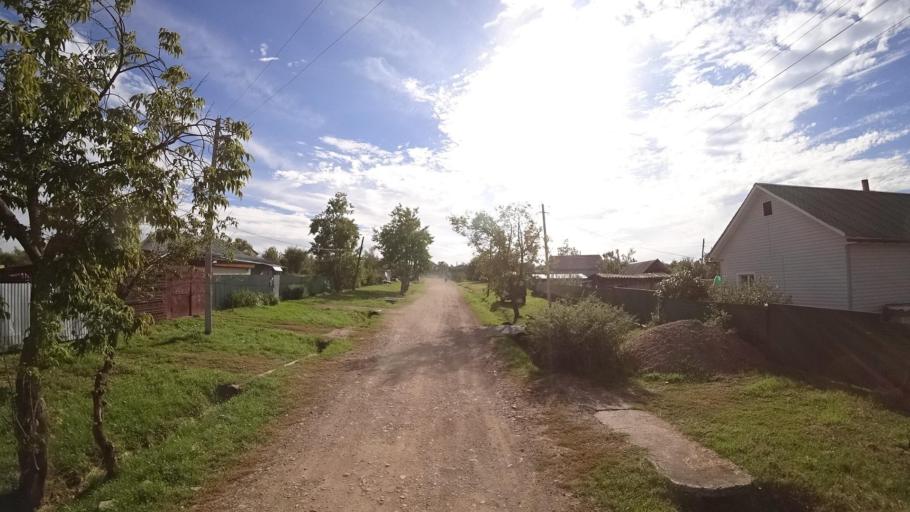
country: RU
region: Primorskiy
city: Dostoyevka
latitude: 44.3049
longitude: 133.4568
